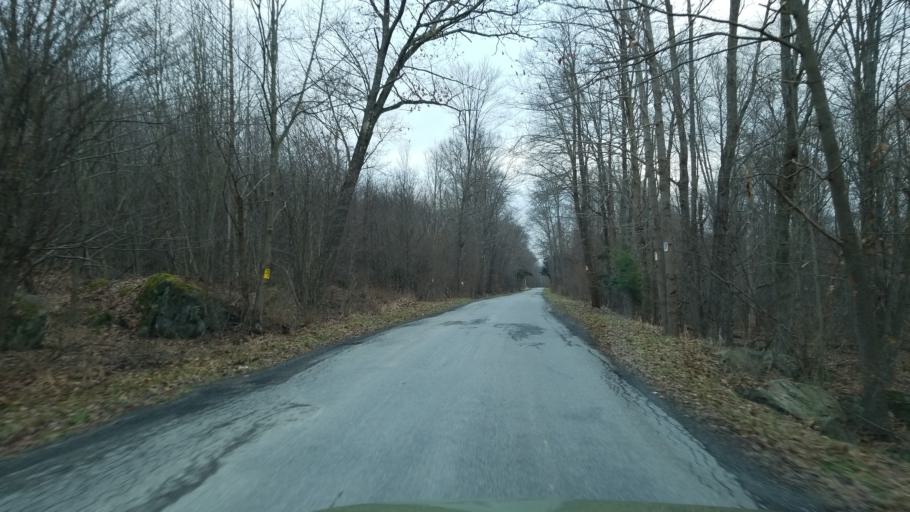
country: US
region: Pennsylvania
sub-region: Jefferson County
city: Falls Creek
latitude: 41.1743
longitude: -78.7914
